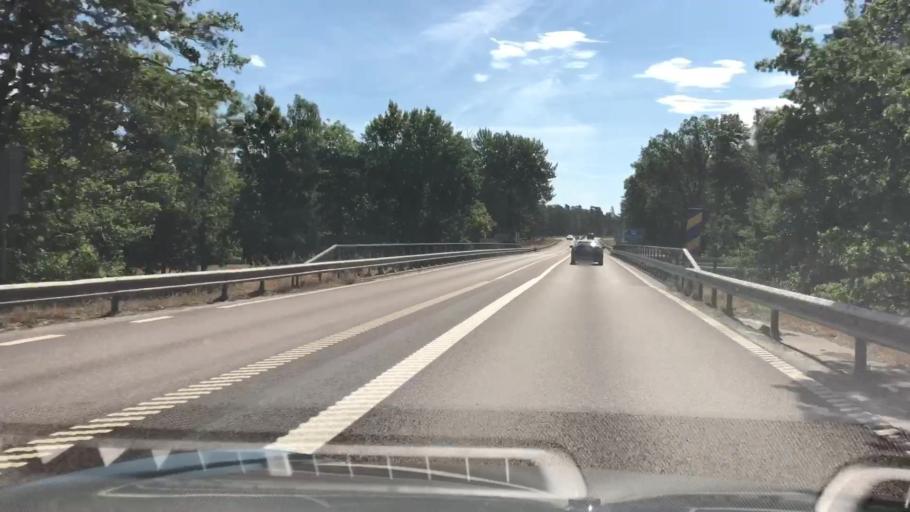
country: SE
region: Kalmar
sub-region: Oskarshamns Kommun
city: Paskallavik
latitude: 57.1266
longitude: 16.4831
